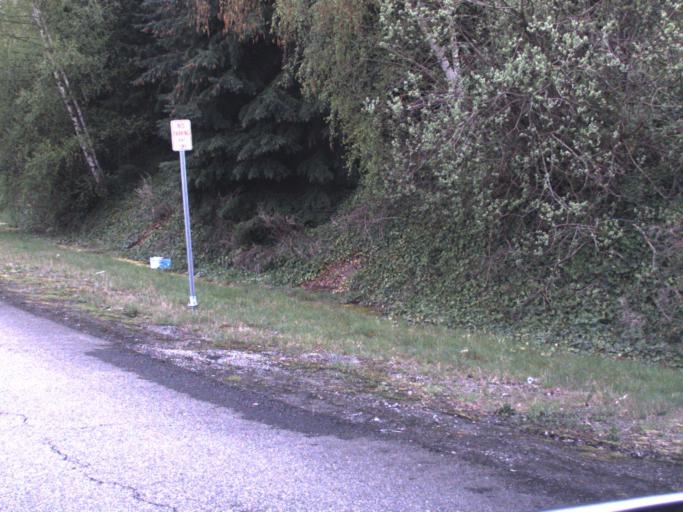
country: US
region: Washington
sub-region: King County
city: Boulevard Park
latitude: 47.4699
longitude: -122.3238
